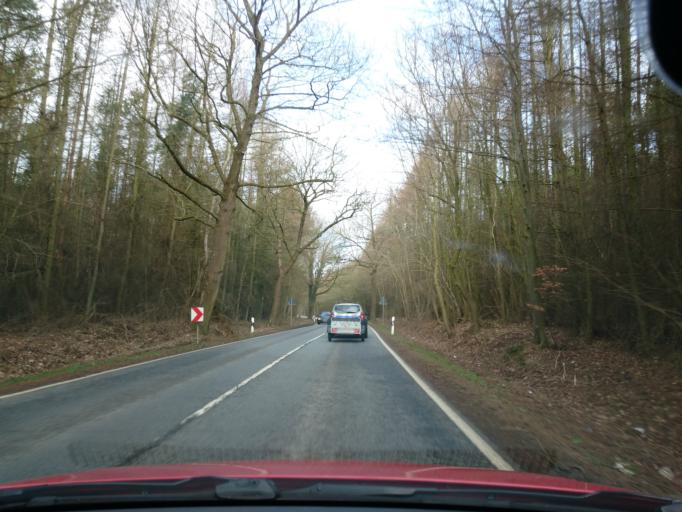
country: DE
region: Mecklenburg-Vorpommern
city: Velgast
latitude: 54.2840
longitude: 12.7989
